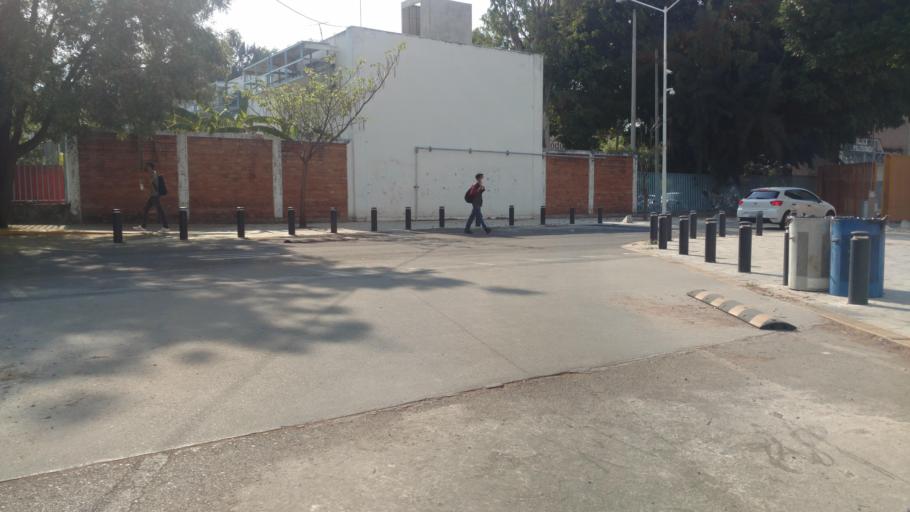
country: MX
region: Jalisco
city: Tlaquepaque
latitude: 20.6590
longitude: -103.3242
